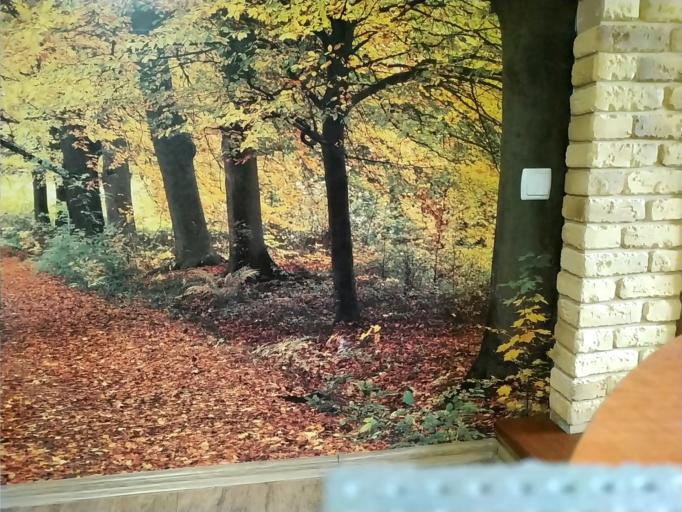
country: RU
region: Tverskaya
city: Kalashnikovo
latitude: 57.2622
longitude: 35.3342
